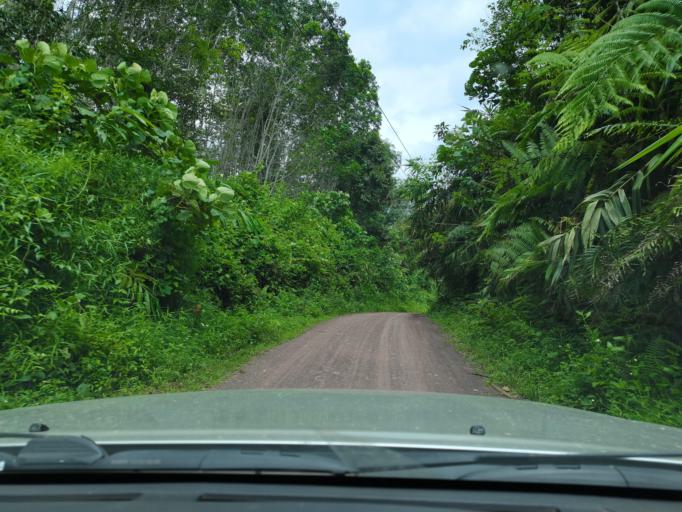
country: LA
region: Loungnamtha
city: Muang Long
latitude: 20.7009
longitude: 101.0261
